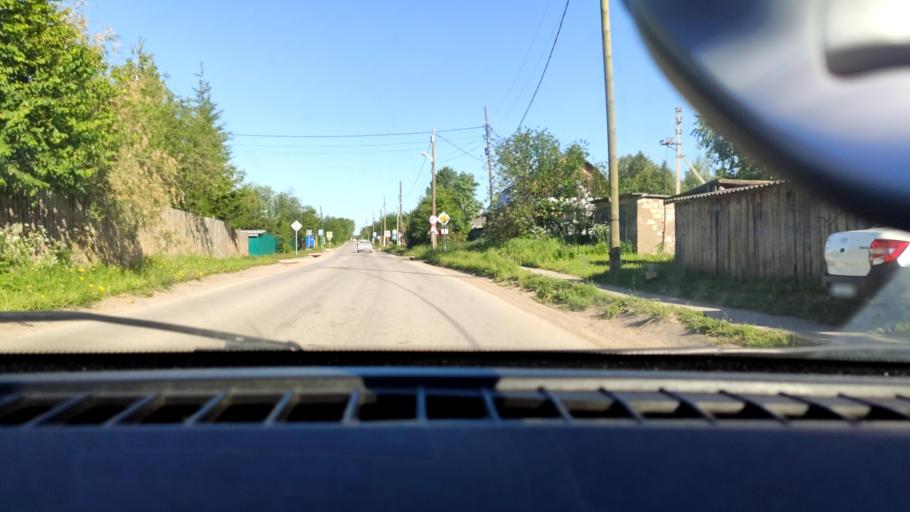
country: RU
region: Perm
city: Novyye Lyady
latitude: 58.1839
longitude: 56.5476
